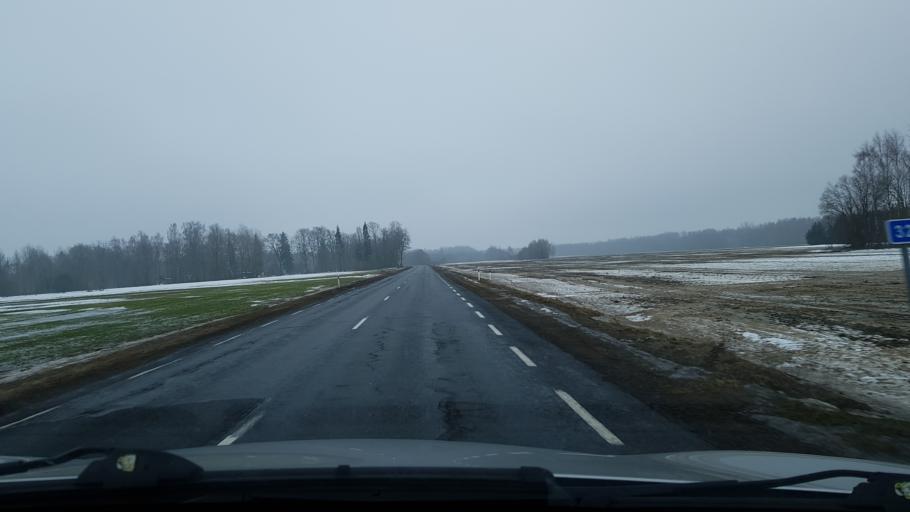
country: EE
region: Valgamaa
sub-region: Torva linn
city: Torva
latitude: 58.1887
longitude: 25.9514
